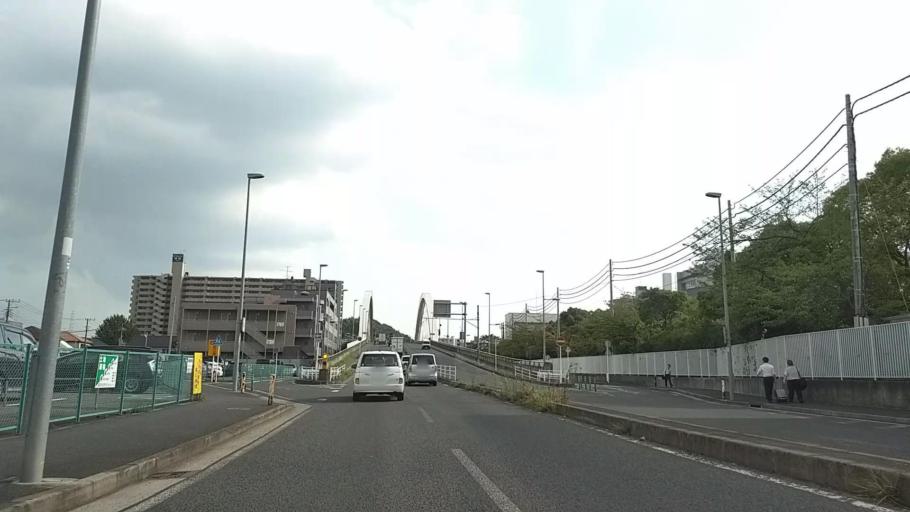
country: JP
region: Kanagawa
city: Yokohama
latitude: 35.5144
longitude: 139.5639
